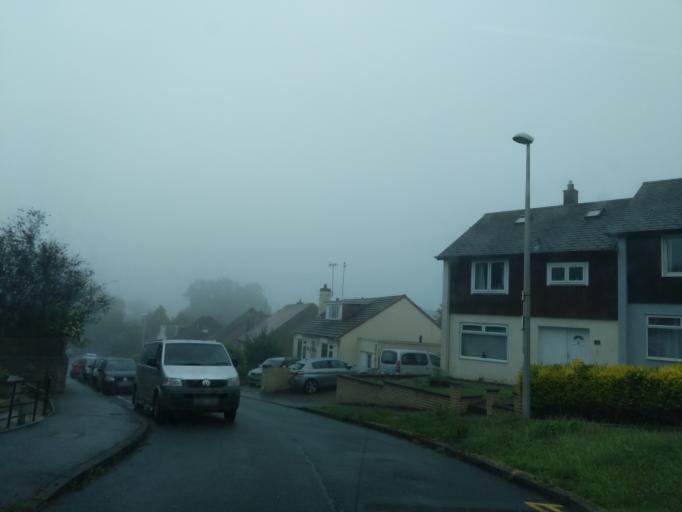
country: GB
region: Scotland
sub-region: West Lothian
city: Seafield
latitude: 55.9438
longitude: -3.1452
